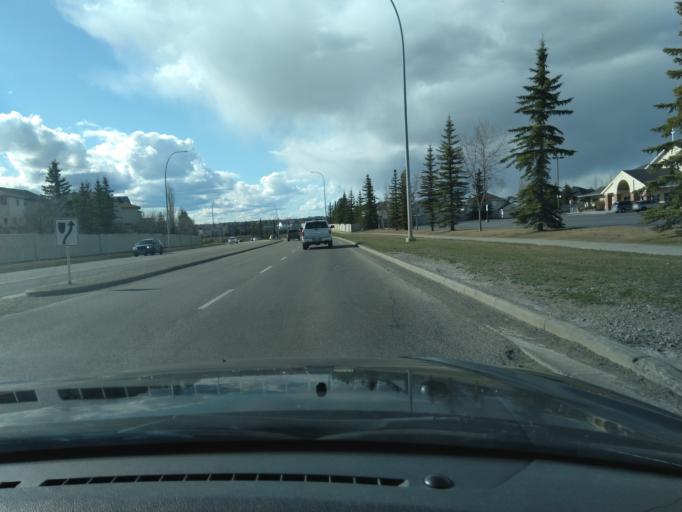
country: CA
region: Alberta
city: Calgary
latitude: 51.1422
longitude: -114.1839
